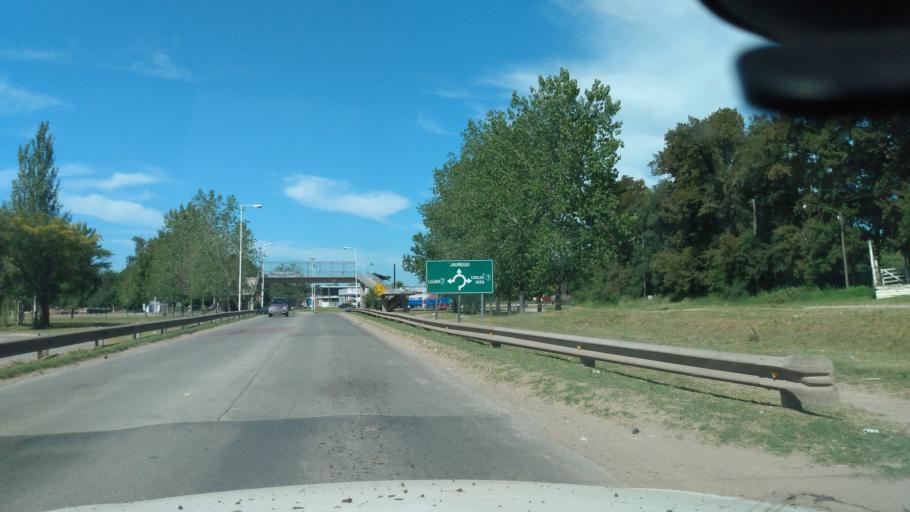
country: AR
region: Buenos Aires
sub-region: Partido de Lujan
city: Lujan
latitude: -34.5490
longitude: -59.1248
